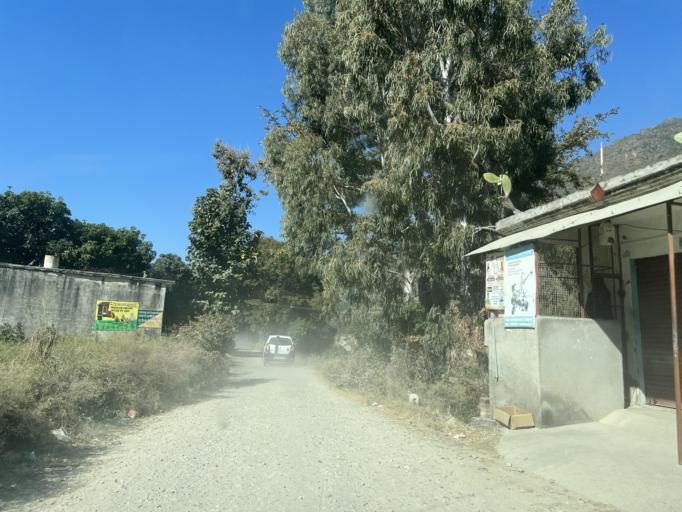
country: IN
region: Uttarakhand
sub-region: Almora
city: Ranikhet
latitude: 29.5523
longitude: 79.3876
